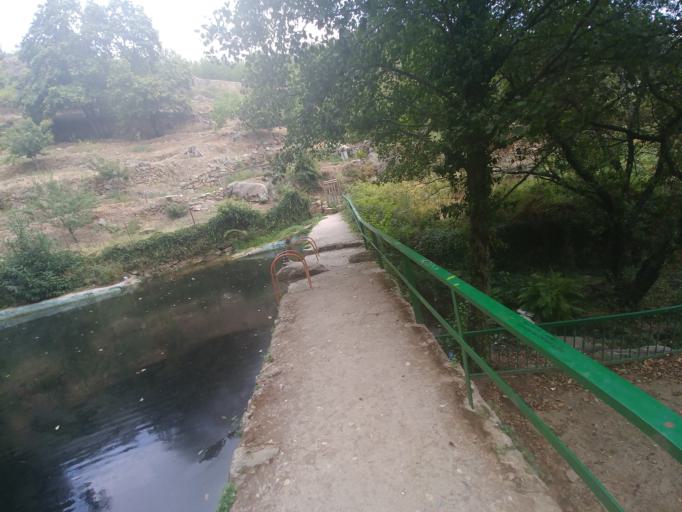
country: ES
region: Extremadura
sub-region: Provincia de Caceres
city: Cabezabellosa
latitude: 40.1357
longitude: -5.9497
